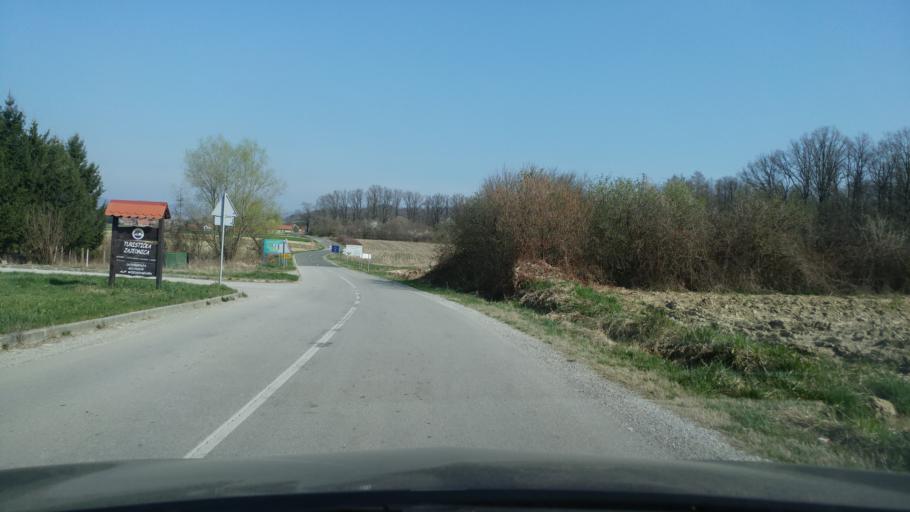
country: HR
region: Zagrebacka
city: Pojatno
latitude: 45.9685
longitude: 15.7375
